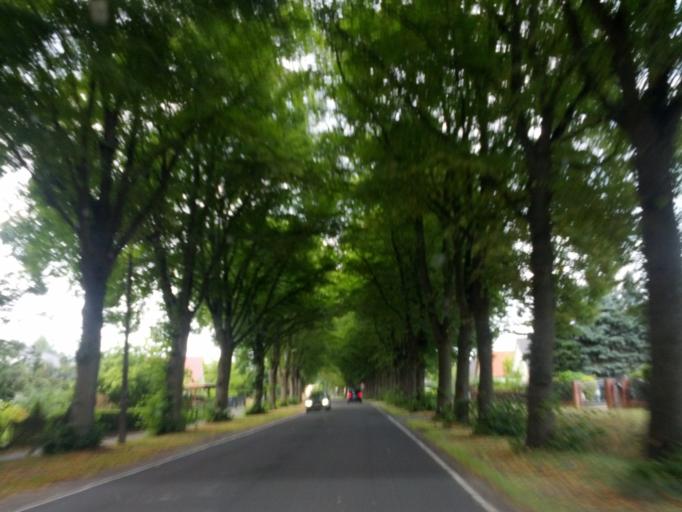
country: DE
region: Brandenburg
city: Kremmen
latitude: 52.7375
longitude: 12.9540
